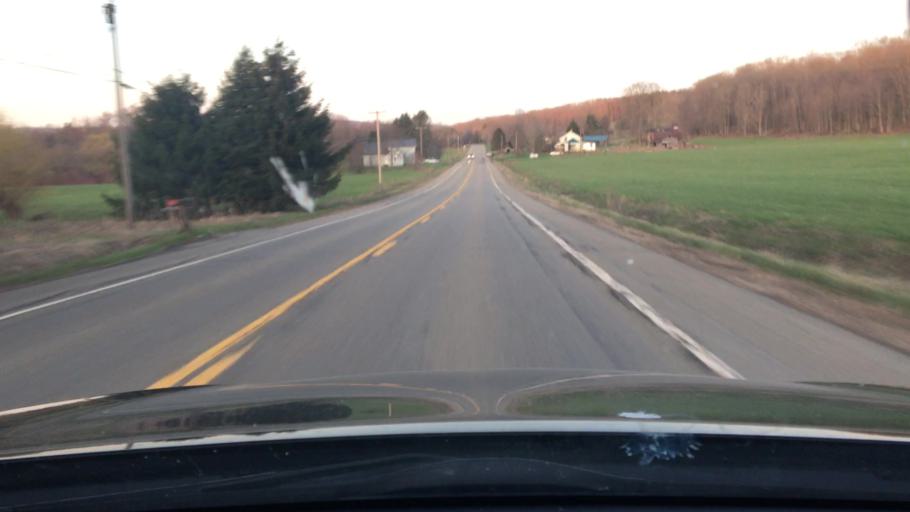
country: US
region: New York
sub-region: Cattaraugus County
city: Randolph
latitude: 42.1819
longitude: -78.9219
